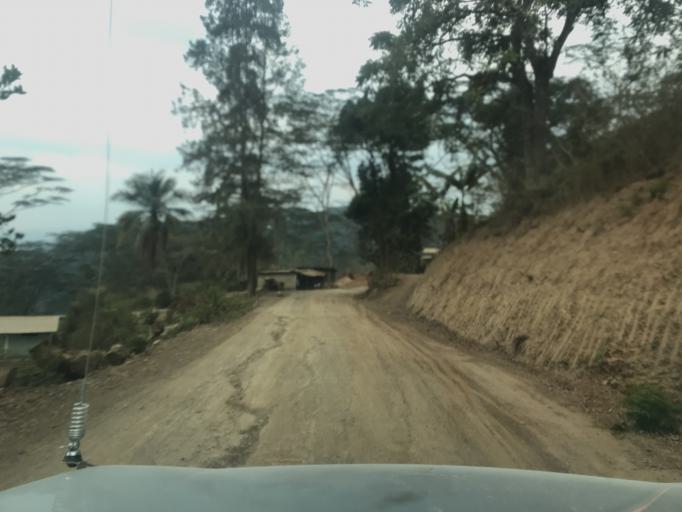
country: TL
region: Ermera
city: Gleno
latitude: -8.7606
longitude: 125.4295
